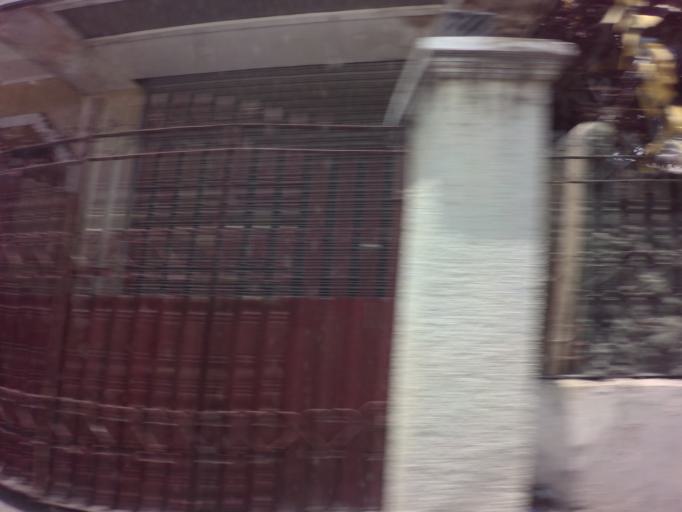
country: PH
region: Calabarzon
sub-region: Province of Laguna
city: San Pedro
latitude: 14.3901
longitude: 121.0493
